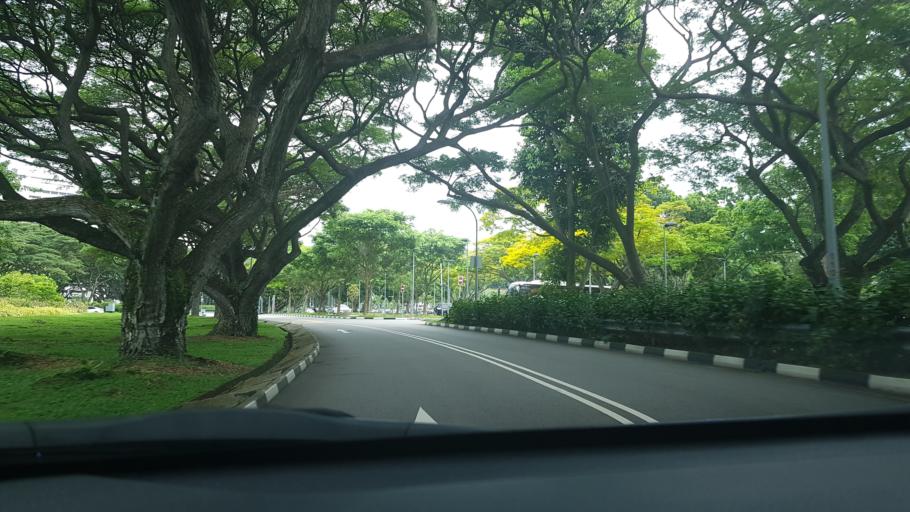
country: SG
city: Singapore
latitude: 1.2999
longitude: 103.9106
